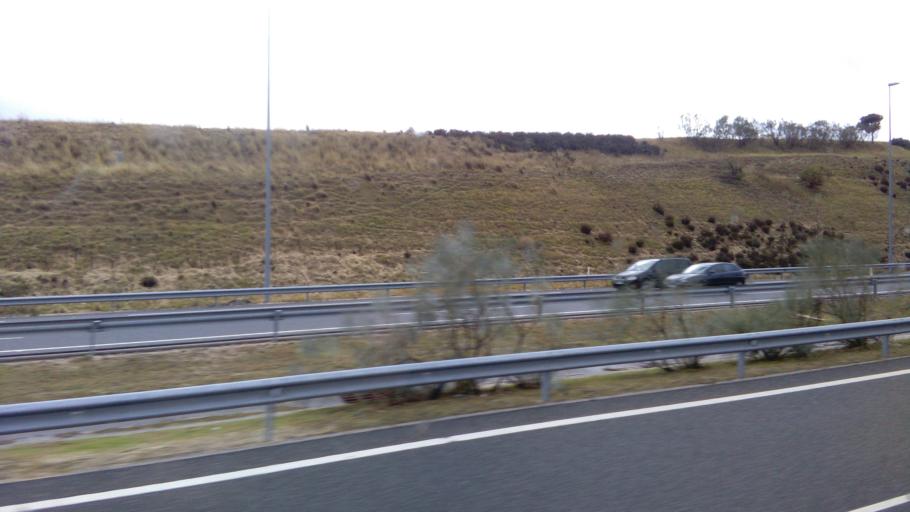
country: ES
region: Madrid
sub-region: Provincia de Madrid
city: Alcorcon
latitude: 40.3426
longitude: -3.7930
